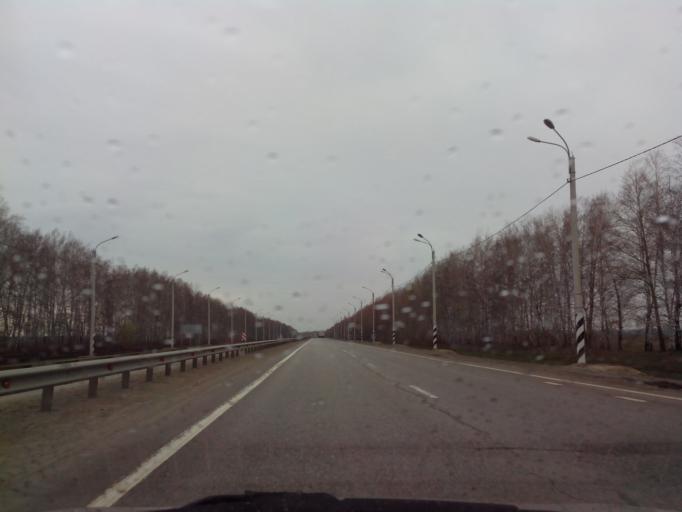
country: RU
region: Tambov
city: Selezni
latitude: 52.7610
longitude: 41.1305
